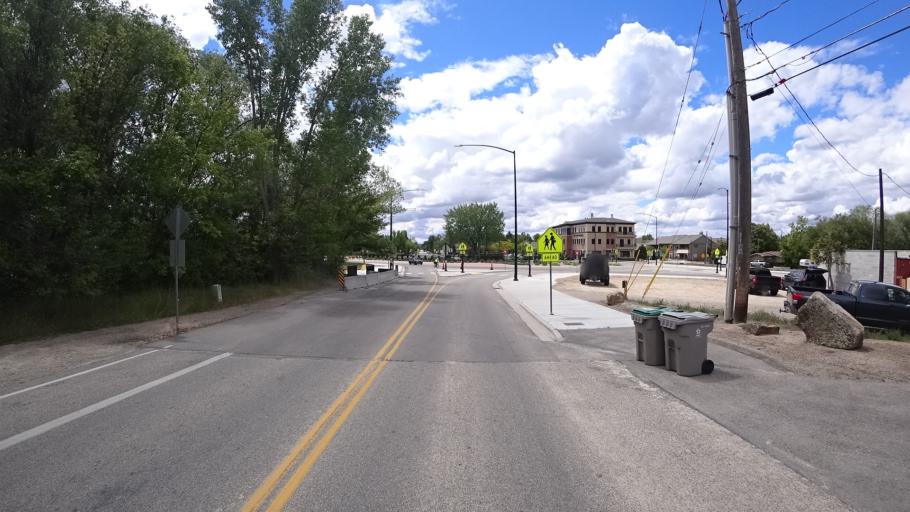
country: US
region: Idaho
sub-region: Ada County
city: Garden City
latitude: 43.6563
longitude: -116.2334
